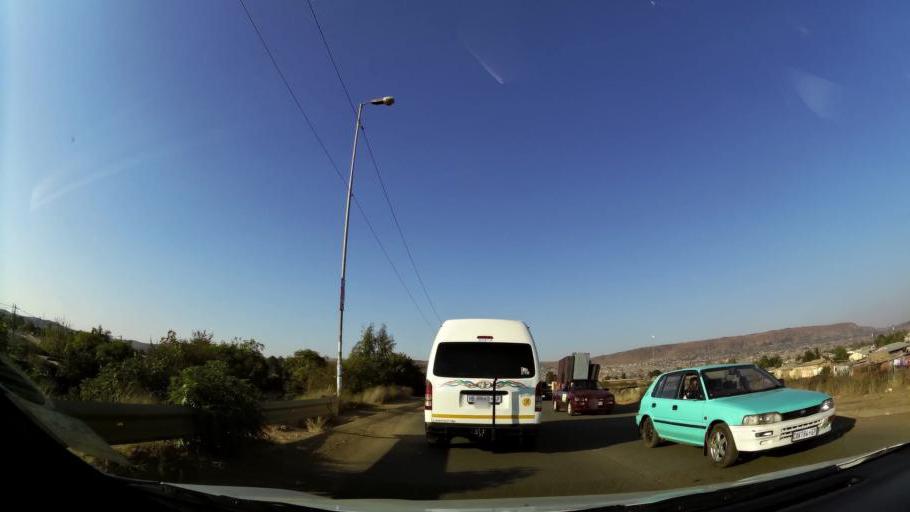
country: ZA
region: Gauteng
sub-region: City of Tshwane Metropolitan Municipality
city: Cullinan
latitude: -25.7107
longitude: 28.4102
